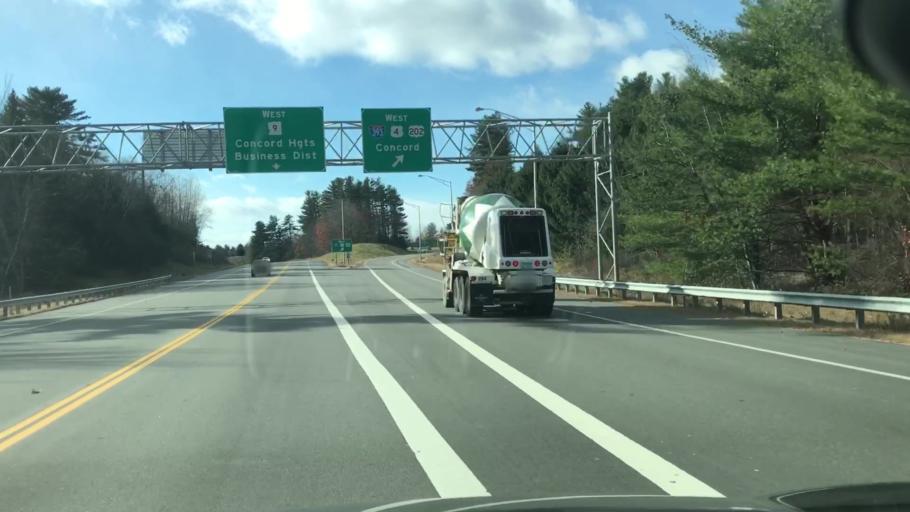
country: US
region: New Hampshire
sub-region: Merrimack County
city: Chichester
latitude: 43.2435
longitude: -71.4508
